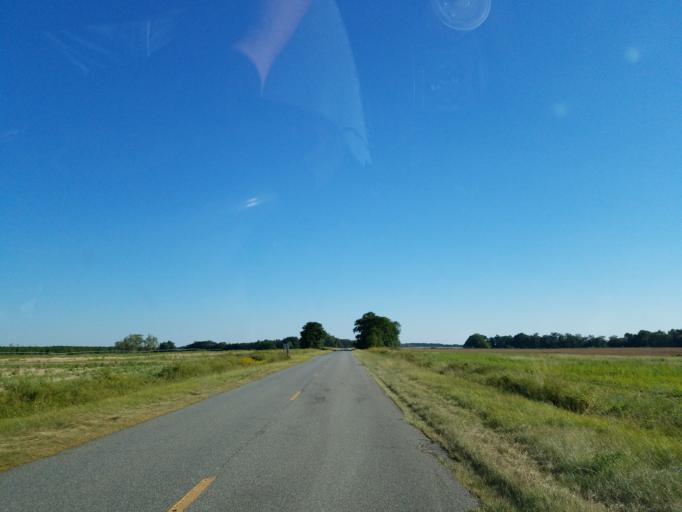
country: US
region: Georgia
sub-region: Dooly County
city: Vienna
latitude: 32.0359
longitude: -83.9443
